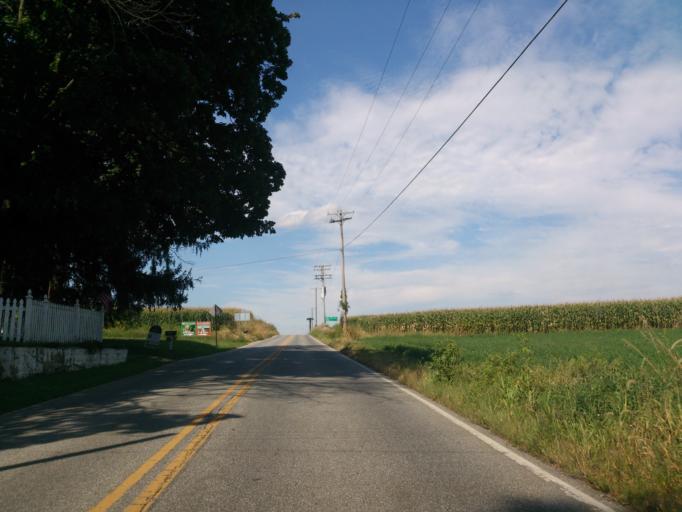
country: US
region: Pennsylvania
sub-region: York County
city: Susquehanna Trails
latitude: 39.7698
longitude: -76.4663
